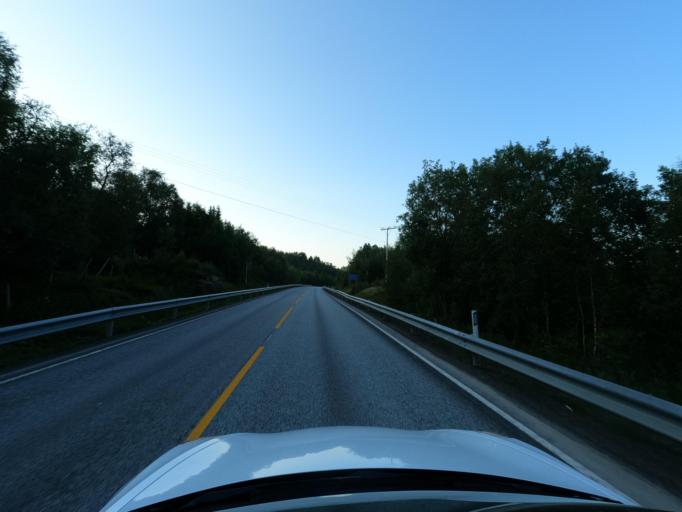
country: NO
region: Troms
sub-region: Harstad
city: Harstad
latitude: 68.7353
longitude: 16.5534
